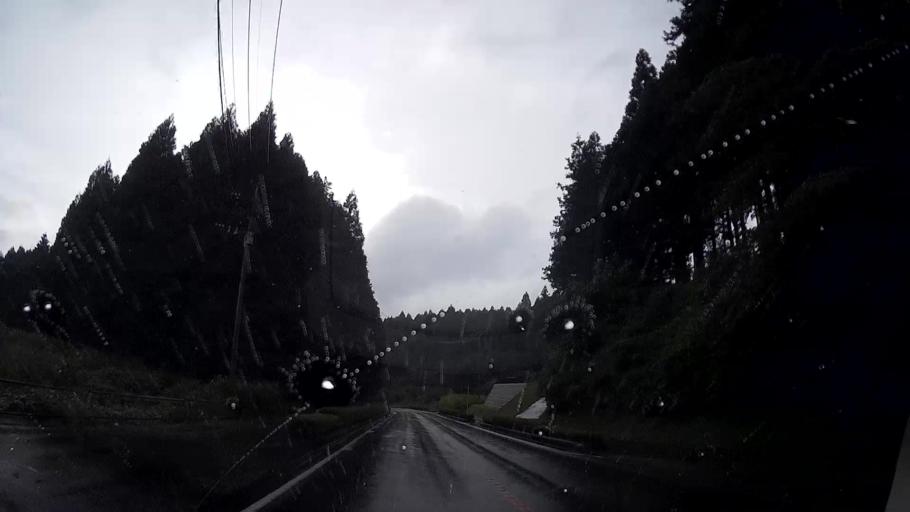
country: JP
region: Kumamoto
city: Aso
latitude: 32.8561
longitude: 131.0150
